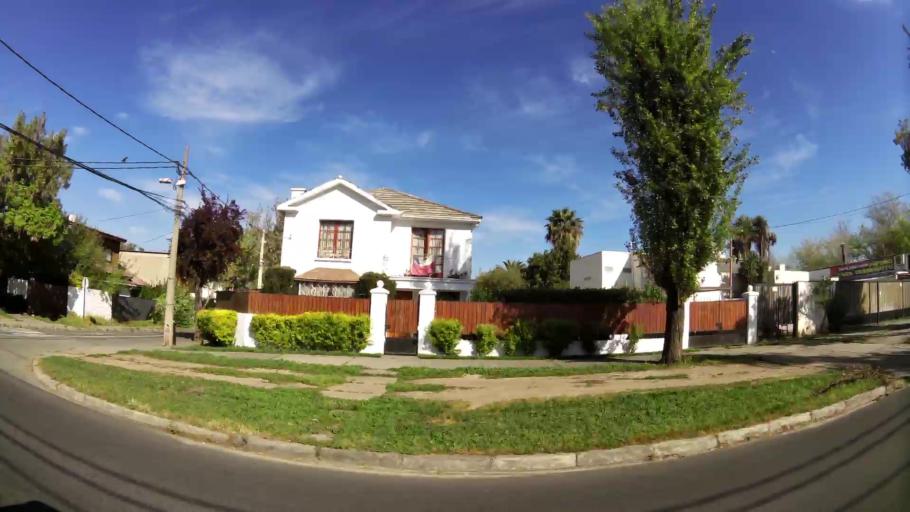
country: CL
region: Santiago Metropolitan
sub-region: Provincia de Santiago
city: Villa Presidente Frei, Nunoa, Santiago, Chile
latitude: -33.4317
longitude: -70.5573
